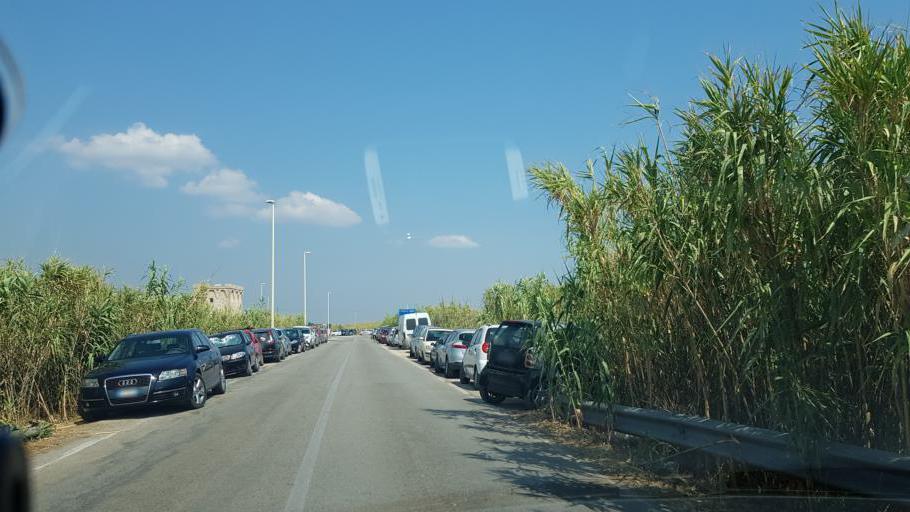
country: IT
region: Apulia
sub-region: Provincia di Taranto
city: Maruggio
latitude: 40.3041
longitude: 17.6331
